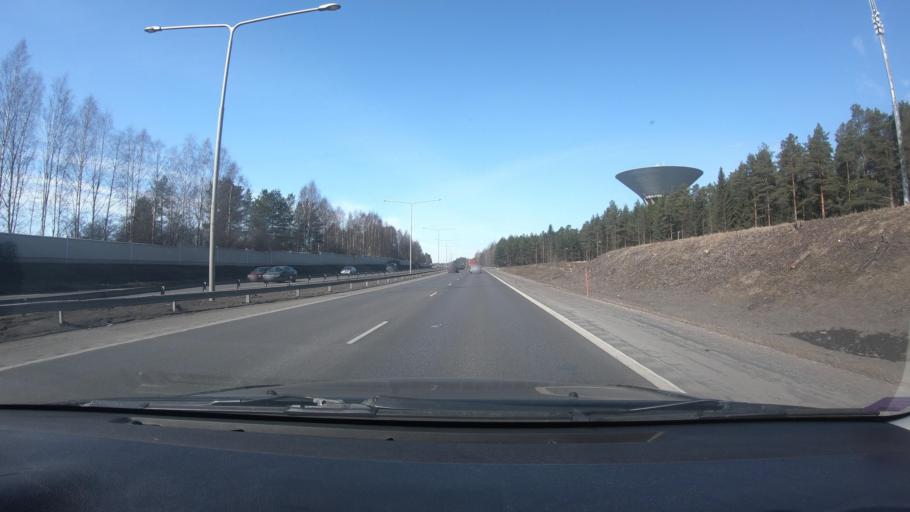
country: FI
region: Northern Ostrobothnia
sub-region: Oulu
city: Oulu
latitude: 65.0350
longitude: 25.4881
